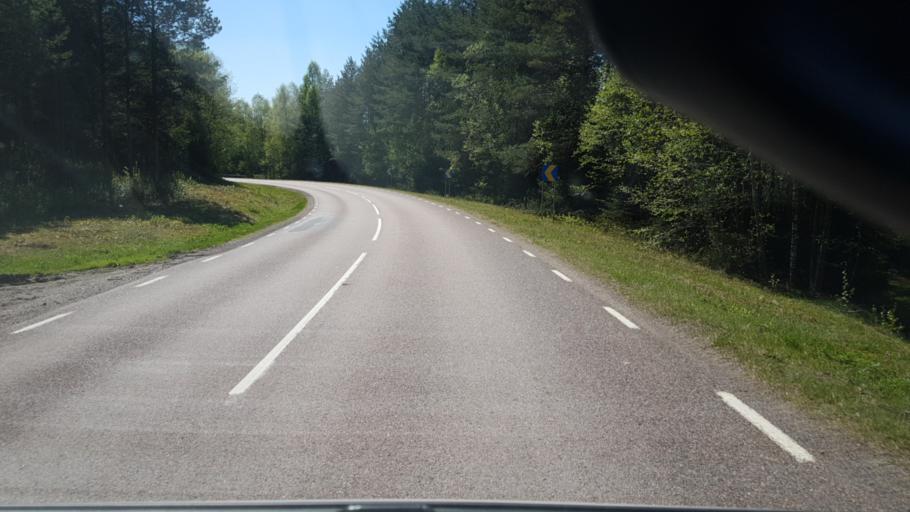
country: SE
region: Vaermland
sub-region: Eda Kommun
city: Amotfors
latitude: 59.8615
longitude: 12.5460
